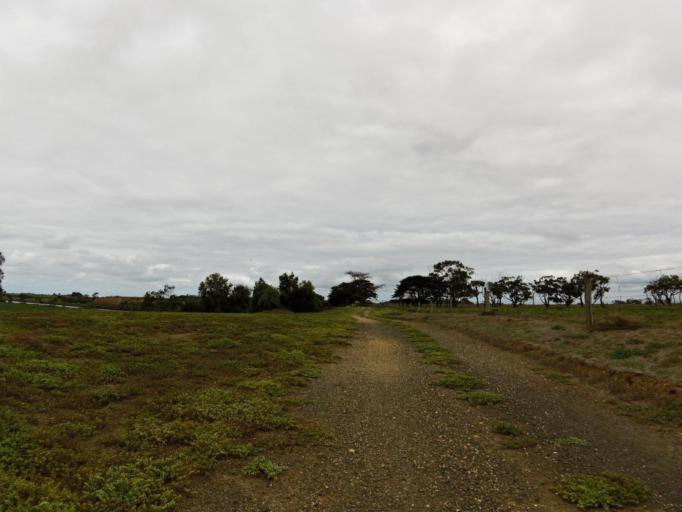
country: AU
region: Victoria
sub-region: Wyndham
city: Werribee
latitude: -37.9477
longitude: 144.6639
